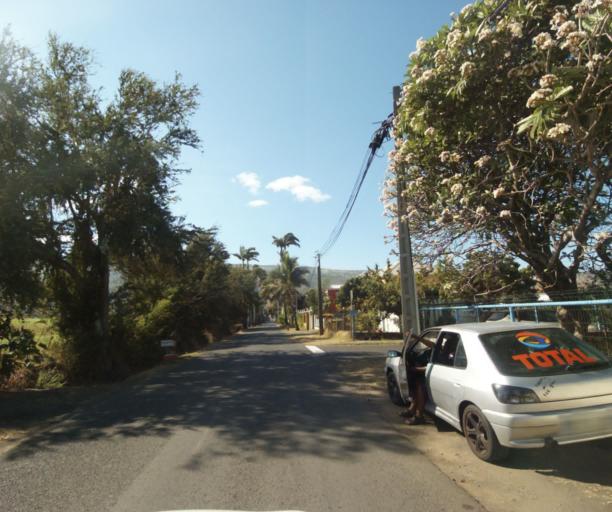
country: RE
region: Reunion
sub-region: Reunion
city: Saint-Paul
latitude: -20.9827
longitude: 55.2949
